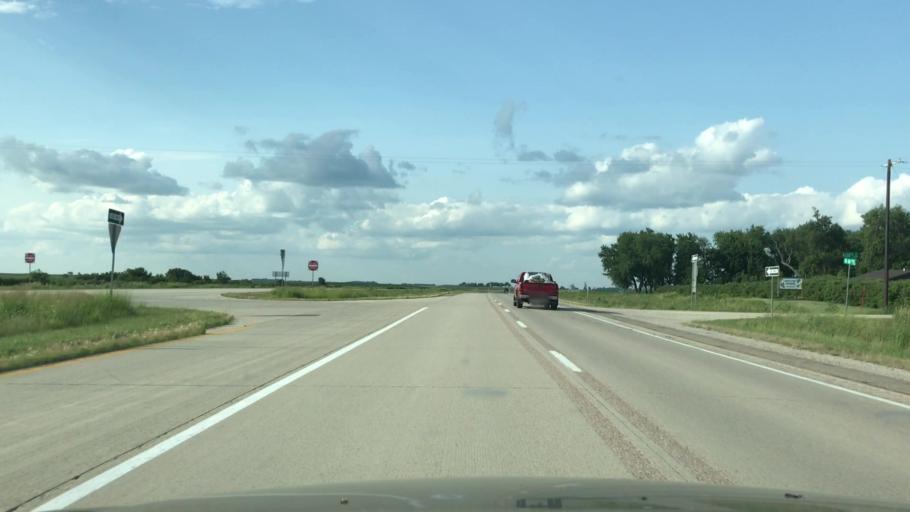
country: US
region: Iowa
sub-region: Osceola County
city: Sibley
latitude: 43.4612
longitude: -95.7122
